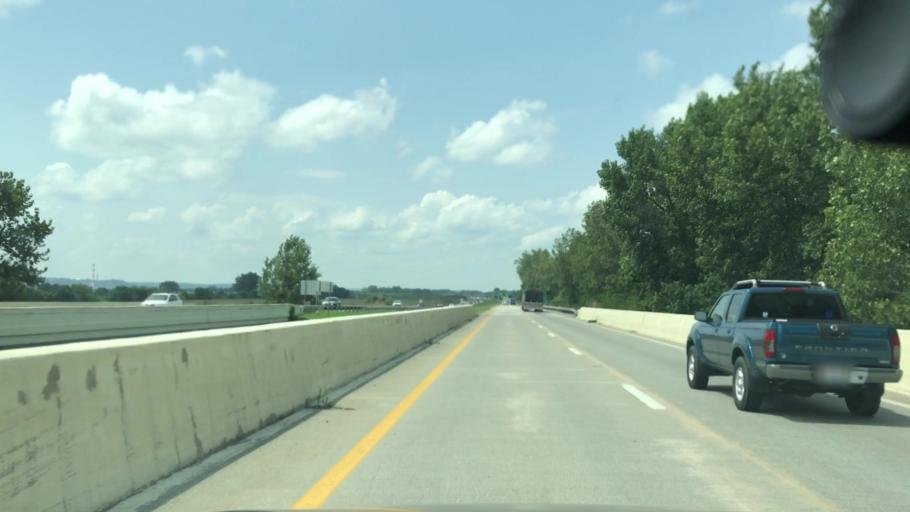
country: US
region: Ohio
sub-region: Ross County
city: Chillicothe
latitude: 39.3075
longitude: -82.9217
